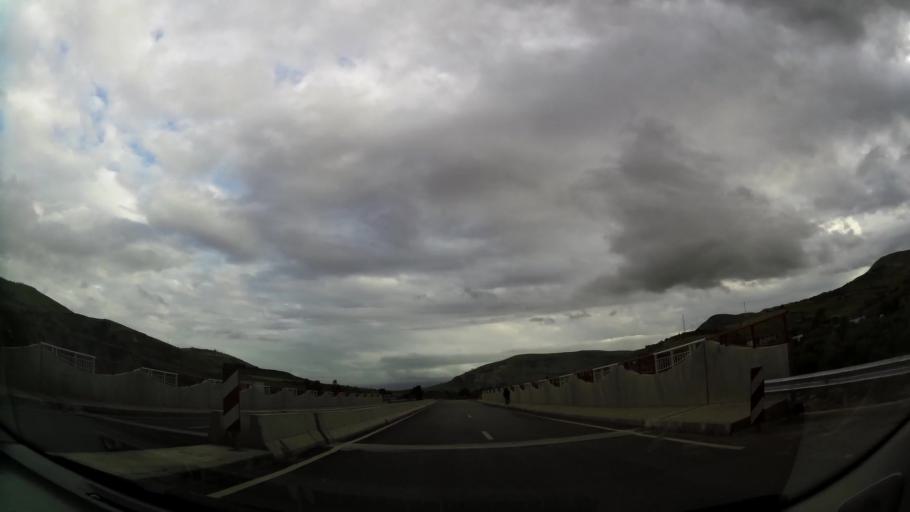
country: MA
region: Taza-Al Hoceima-Taounate
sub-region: Taza
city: Taza
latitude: 34.3100
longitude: -3.9667
